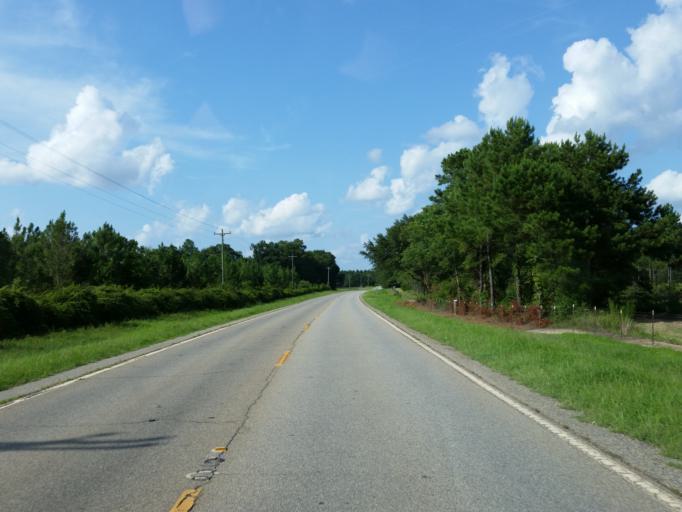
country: US
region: Georgia
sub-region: Lee County
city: Leesburg
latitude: 31.8115
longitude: -84.1156
